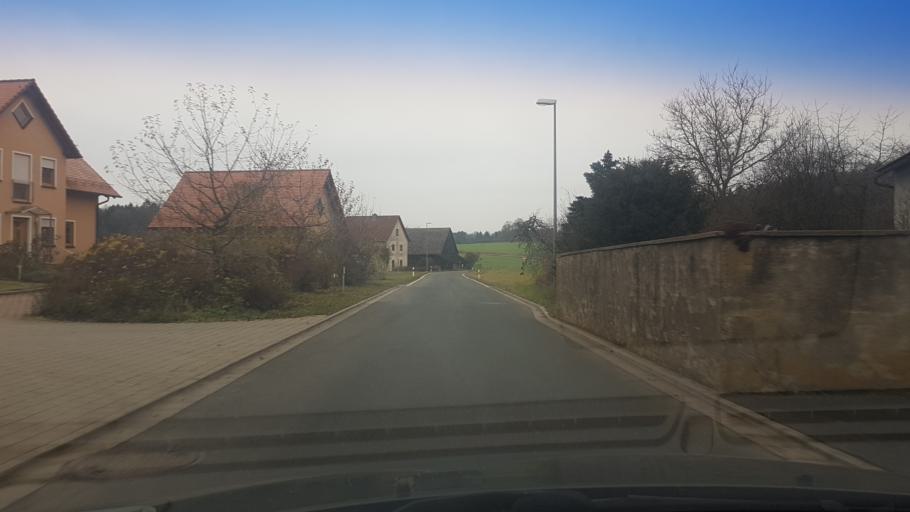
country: DE
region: Bavaria
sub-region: Upper Franconia
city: Stadelhofen
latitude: 50.0182
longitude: 11.2433
